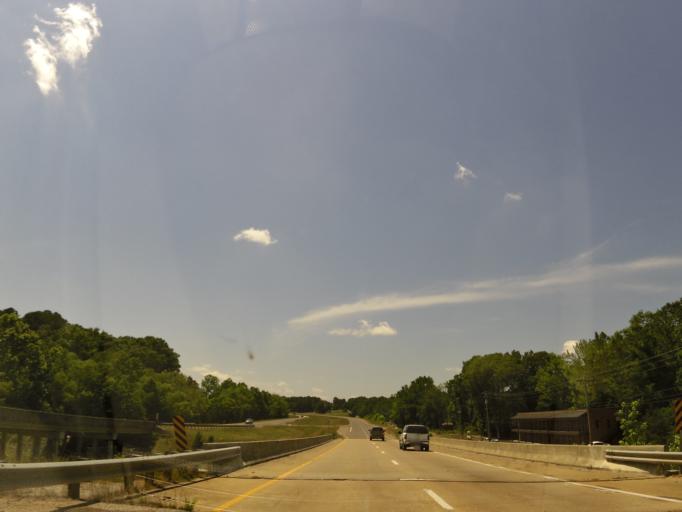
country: US
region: Mississippi
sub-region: Lafayette County
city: Oxford
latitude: 34.3572
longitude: -89.4795
